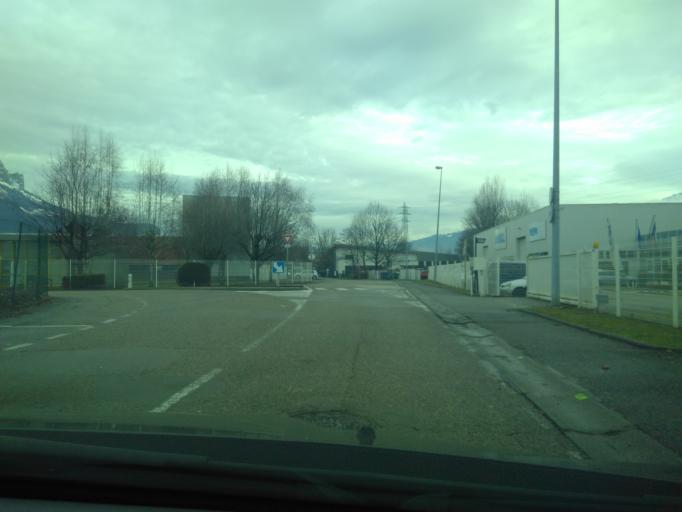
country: FR
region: Rhone-Alpes
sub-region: Departement de l'Isere
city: Montbonnot-Saint-Martin
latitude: 45.2206
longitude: 5.8175
